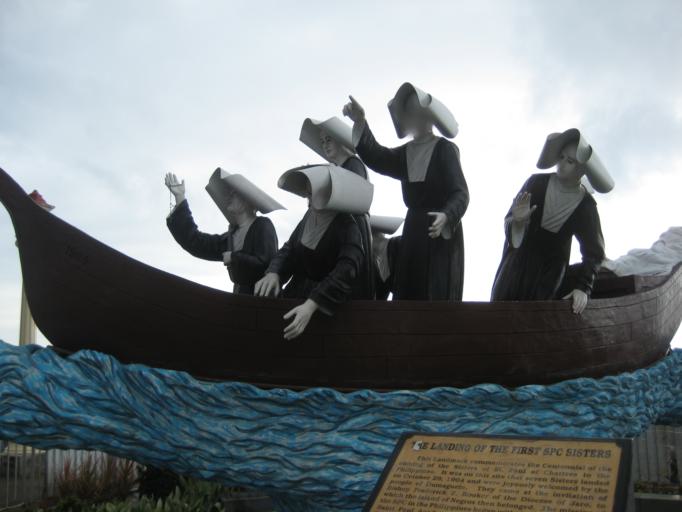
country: PH
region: Central Visayas
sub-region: Province of Negros Oriental
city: Dumaguete
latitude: 9.3081
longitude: 123.3098
